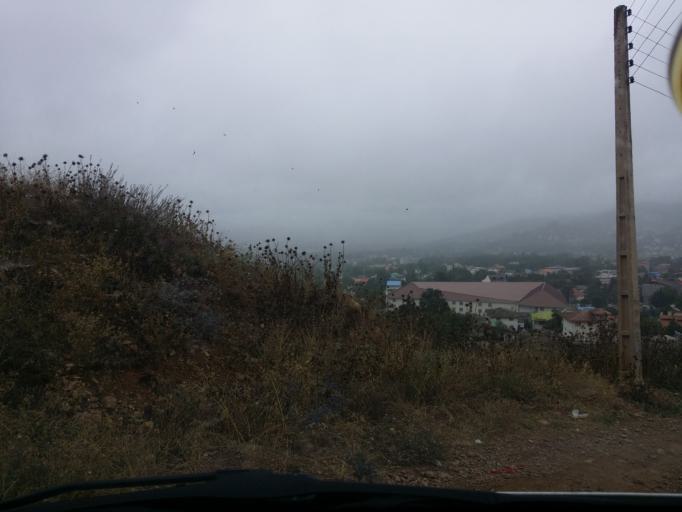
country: IR
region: Mazandaran
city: `Abbasabad
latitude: 36.5101
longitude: 51.1536
